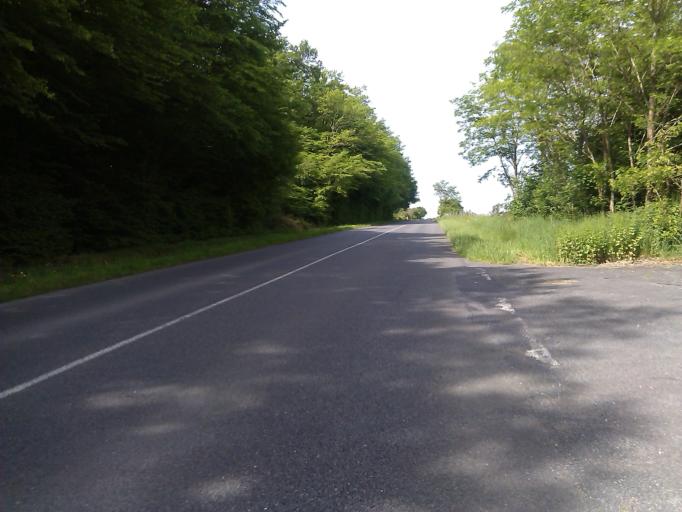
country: FR
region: Auvergne
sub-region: Departement de l'Allier
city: Dompierre-sur-Besbre
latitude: 46.5314
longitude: 3.6295
